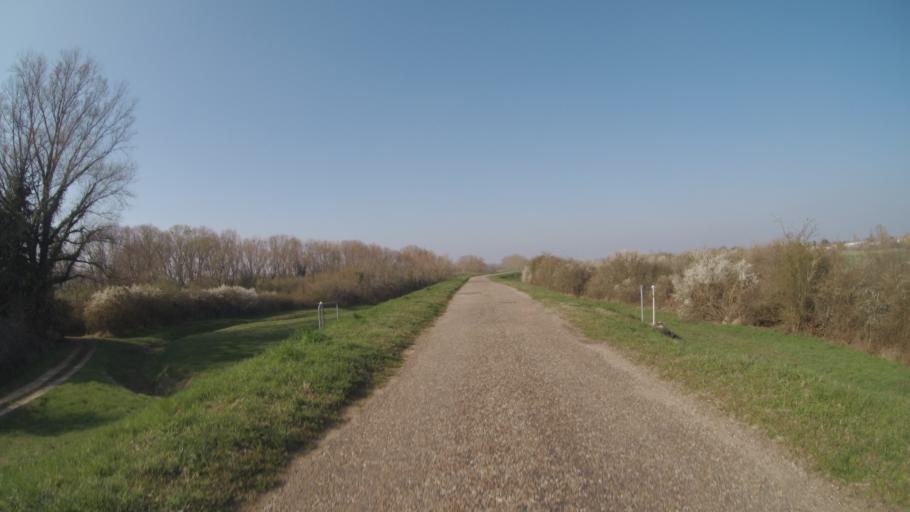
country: FR
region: Centre
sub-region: Departement du Loiret
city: Sandillon
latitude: 47.8701
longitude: 2.0368
